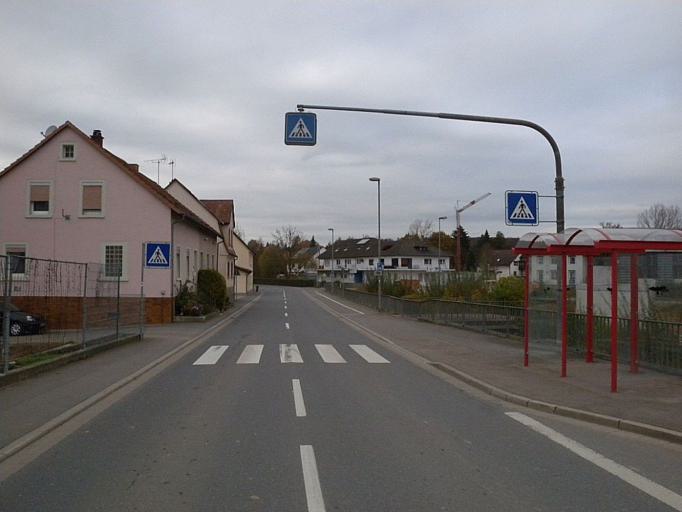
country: DE
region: Baden-Wuerttemberg
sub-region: Karlsruhe Region
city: Neckarbischofsheim
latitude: 49.3205
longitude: 8.9753
